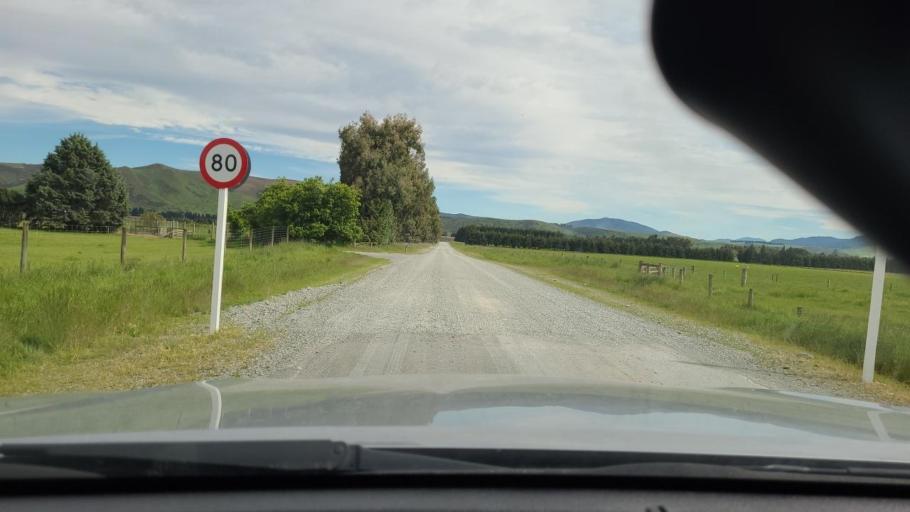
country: NZ
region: Southland
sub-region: Southland District
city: Te Anau
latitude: -45.5367
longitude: 167.9640
